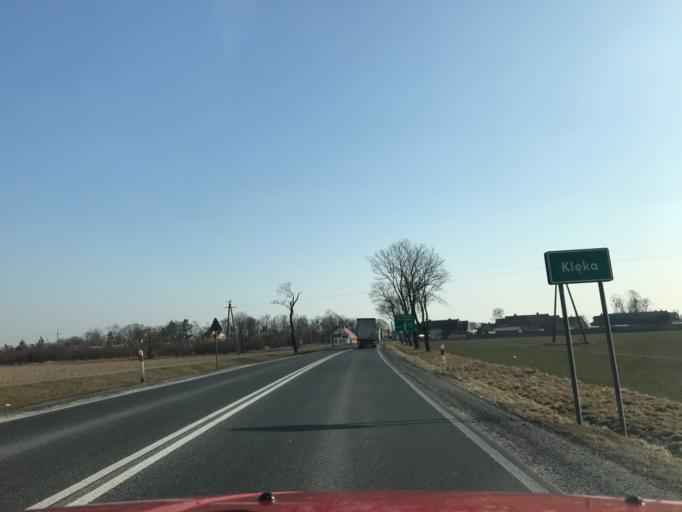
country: PL
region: Greater Poland Voivodeship
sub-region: Powiat sredzki
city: Nowe Miasto nad Warta
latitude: 52.0779
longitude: 17.4173
